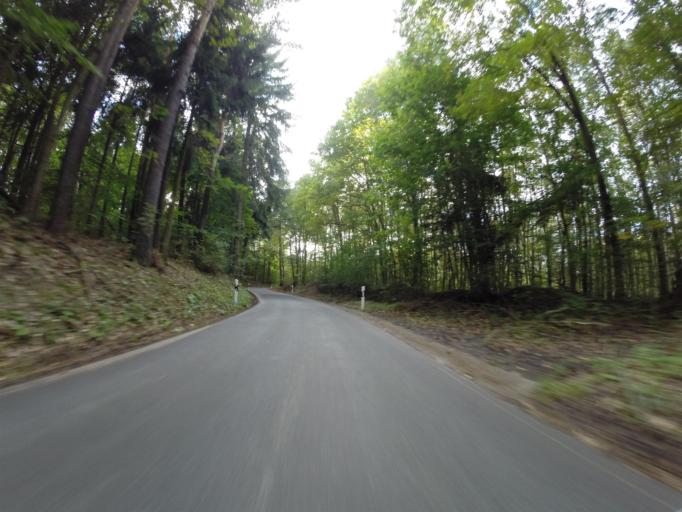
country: DE
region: Thuringia
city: Jena
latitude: 50.9395
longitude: 11.5381
